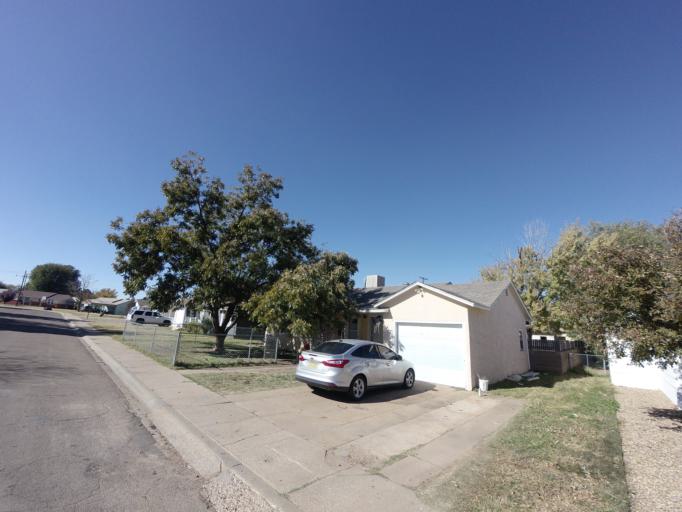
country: US
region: New Mexico
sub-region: Curry County
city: Clovis
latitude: 34.4286
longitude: -103.2038
